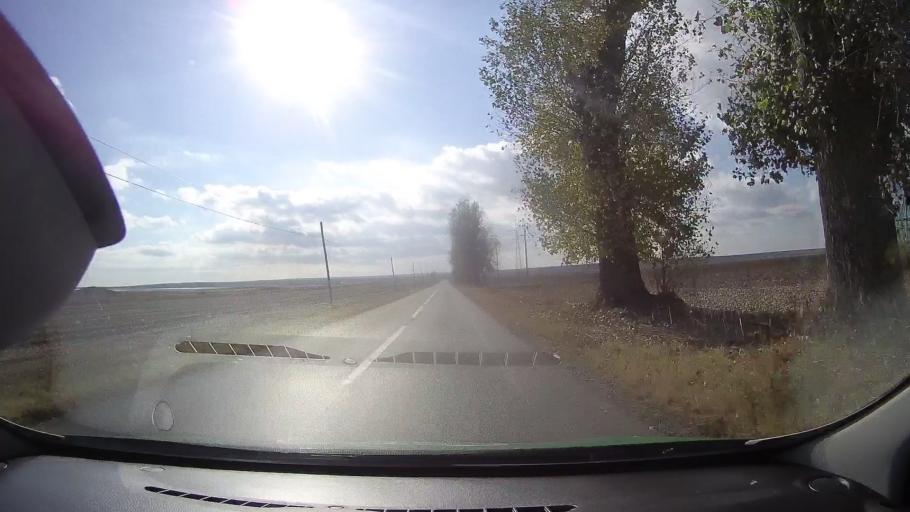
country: RO
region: Constanta
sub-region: Comuna Istria
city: Istria
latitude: 44.5430
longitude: 28.6908
